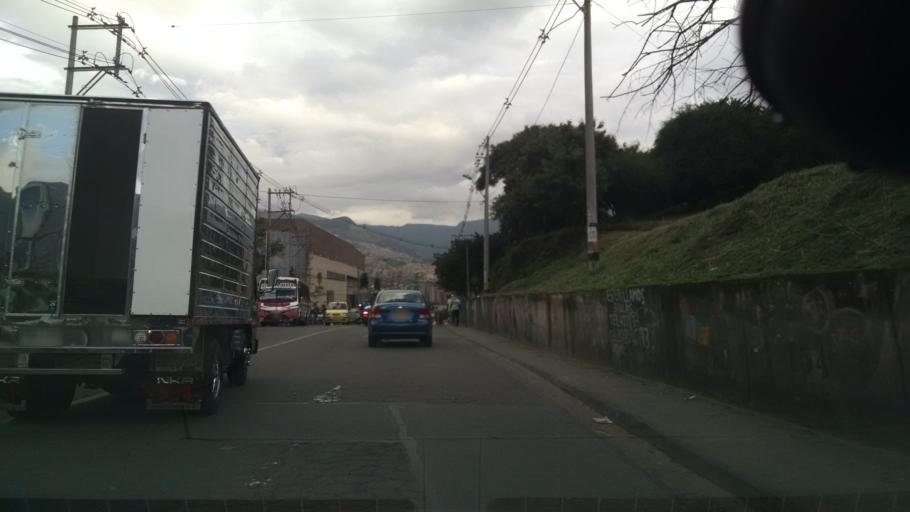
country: CO
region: Antioquia
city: Medellin
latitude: 6.2716
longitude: -75.5789
